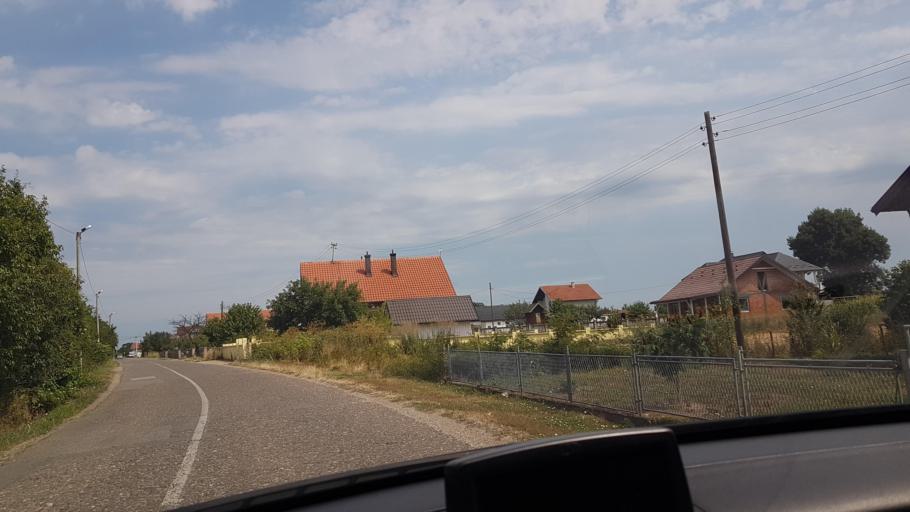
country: BA
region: Republika Srpska
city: Dvorovi
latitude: 44.8093
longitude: 19.2184
